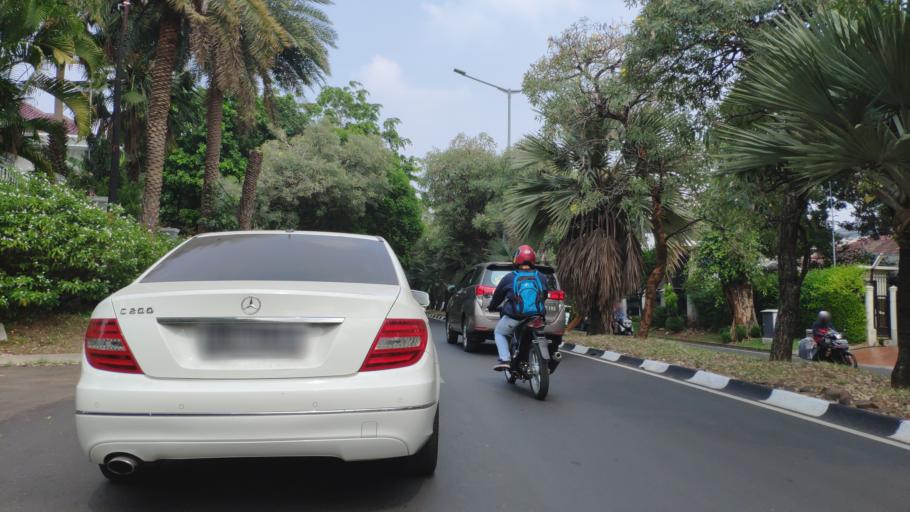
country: ID
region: Banten
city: South Tangerang
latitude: -6.2812
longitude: 106.7834
